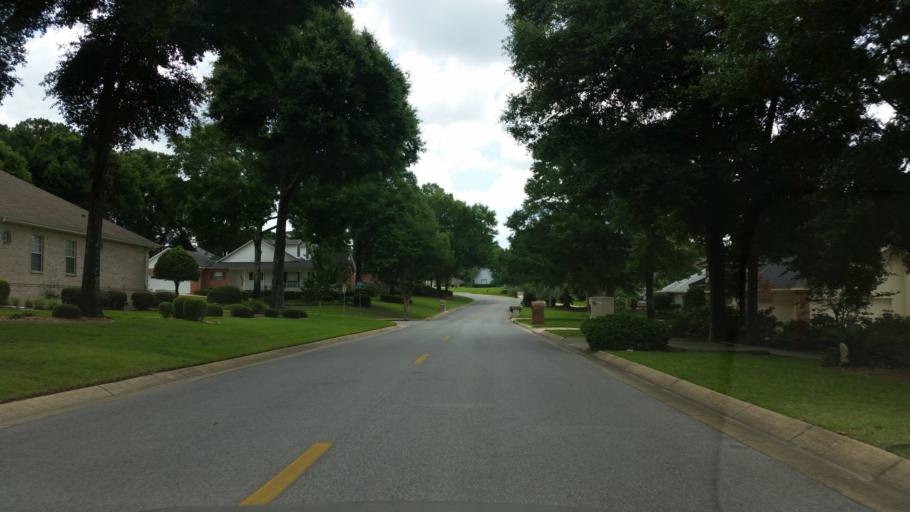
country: US
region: Florida
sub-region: Escambia County
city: Bellview
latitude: 30.4804
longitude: -87.2811
